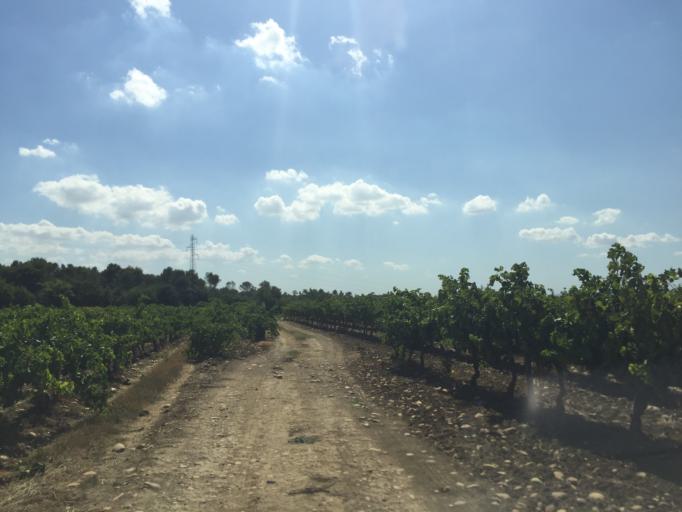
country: FR
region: Provence-Alpes-Cote d'Azur
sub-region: Departement du Vaucluse
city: Bedarrides
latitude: 44.0241
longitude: 4.8929
